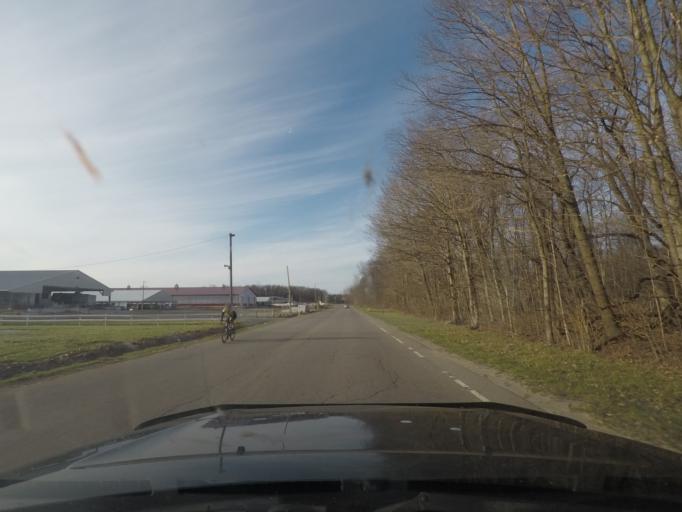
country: US
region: Indiana
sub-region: LaPorte County
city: LaPorte
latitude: 41.5946
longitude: -86.7492
